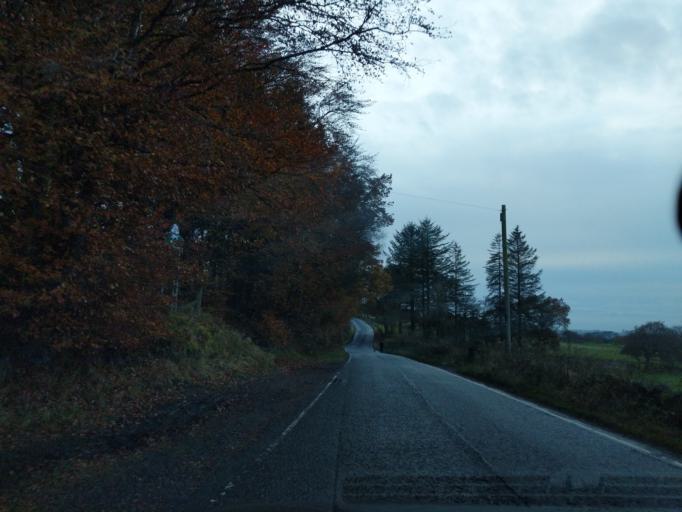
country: GB
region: Scotland
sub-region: West Lothian
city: Linlithgow
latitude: 55.9414
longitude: -3.6198
